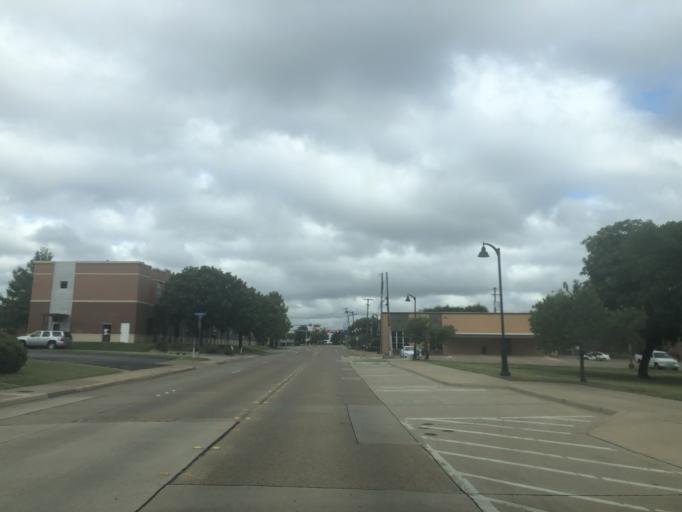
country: US
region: Texas
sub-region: Dallas County
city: Duncanville
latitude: 32.6518
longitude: -96.9066
